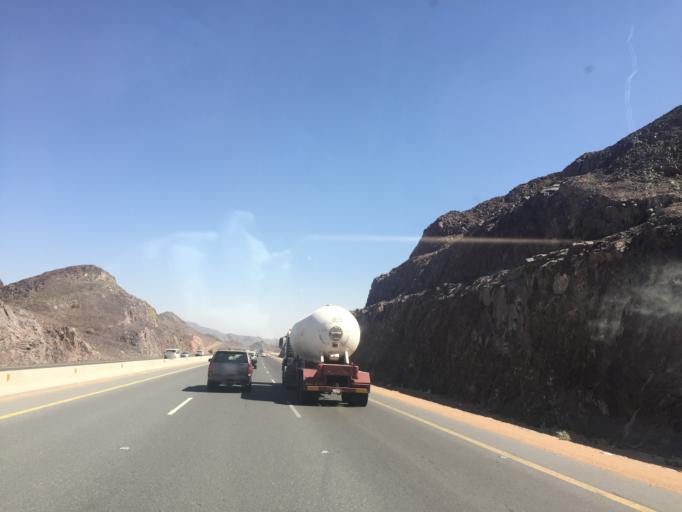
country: SA
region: Al Madinah al Munawwarah
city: Sultanah
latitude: 24.3172
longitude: 39.4363
